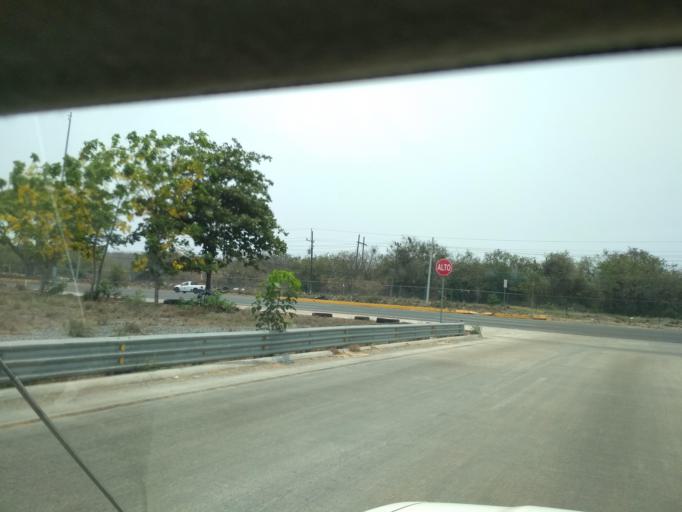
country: MX
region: Veracruz
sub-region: Veracruz
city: Delfino Victoria (Santa Fe)
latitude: 19.1796
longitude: -96.2489
